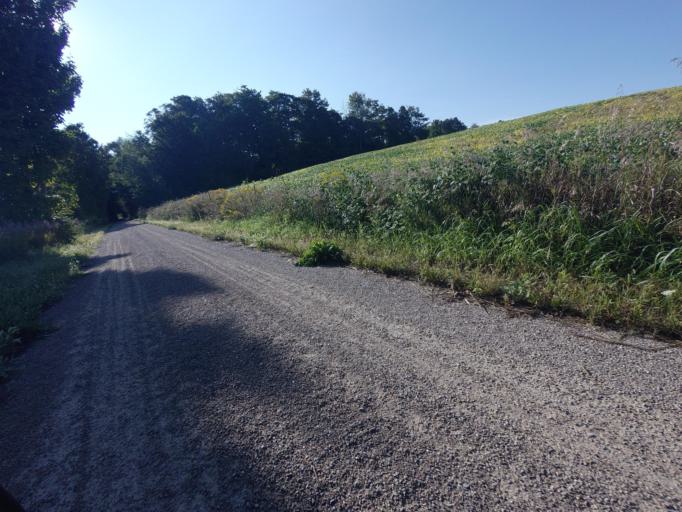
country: CA
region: Ontario
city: Huron East
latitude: 43.7419
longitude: -81.4811
